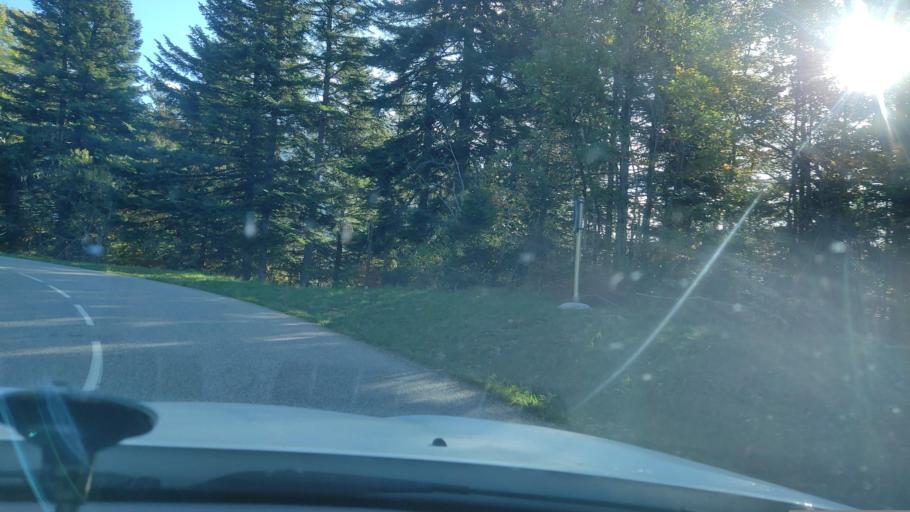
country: FR
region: Rhone-Alpes
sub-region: Departement de la Savoie
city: Beaufort
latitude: 45.7326
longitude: 6.5607
